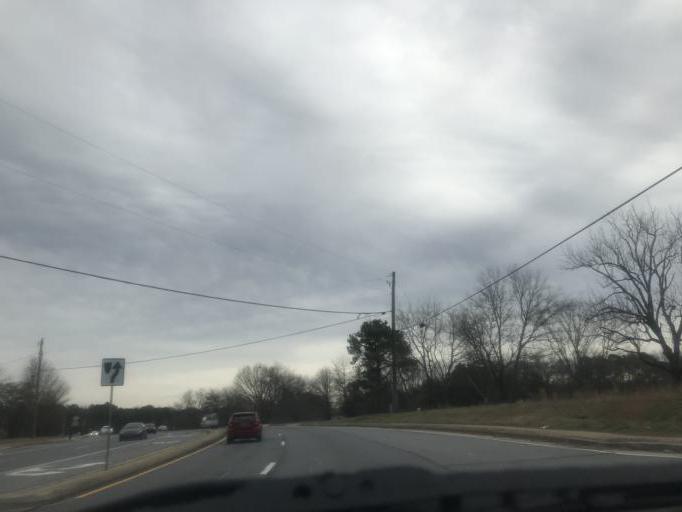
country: US
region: Georgia
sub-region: Gwinnett County
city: Buford
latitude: 34.0680
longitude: -83.9565
